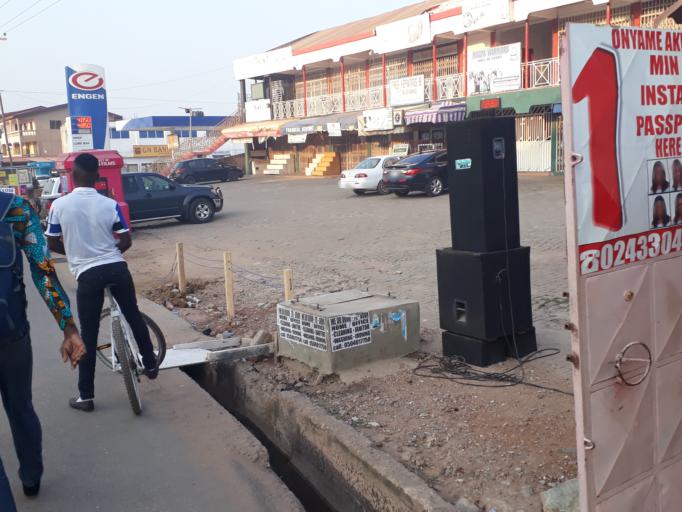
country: GH
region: Greater Accra
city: Dome
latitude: 5.6421
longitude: -0.2385
